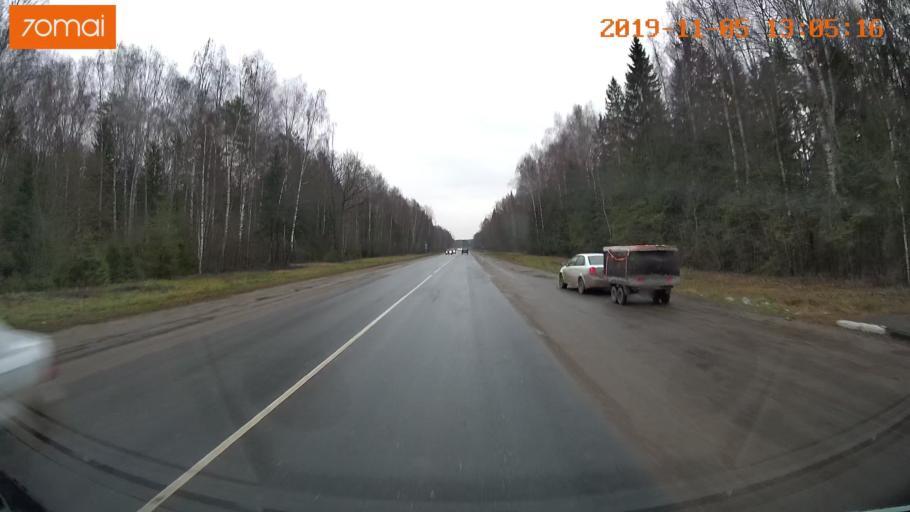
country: RU
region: Ivanovo
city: Kitovo
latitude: 56.8837
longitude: 41.2391
